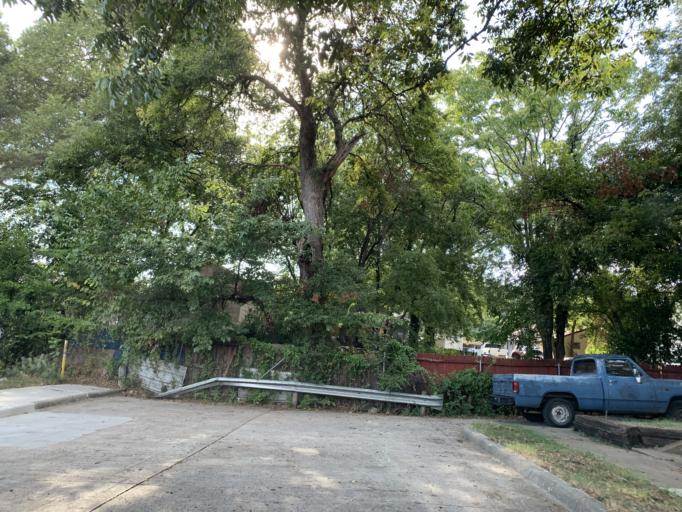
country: US
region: Texas
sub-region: Dallas County
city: Cockrell Hill
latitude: 32.7382
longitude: -96.8351
